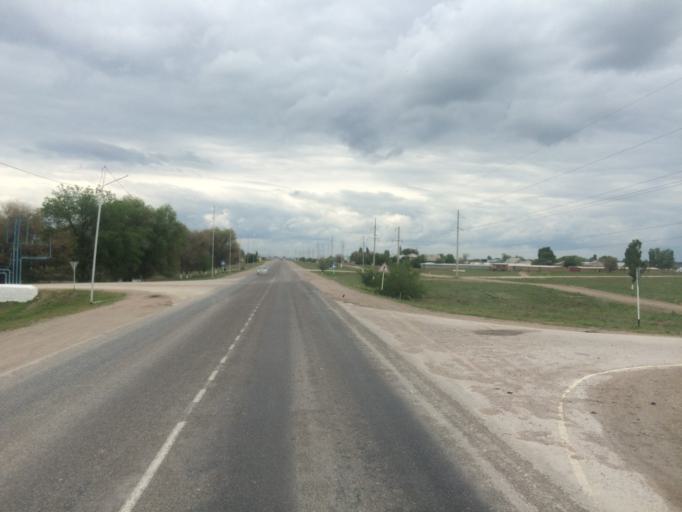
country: KG
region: Chuy
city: Sokuluk
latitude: 43.2505
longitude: 74.2879
